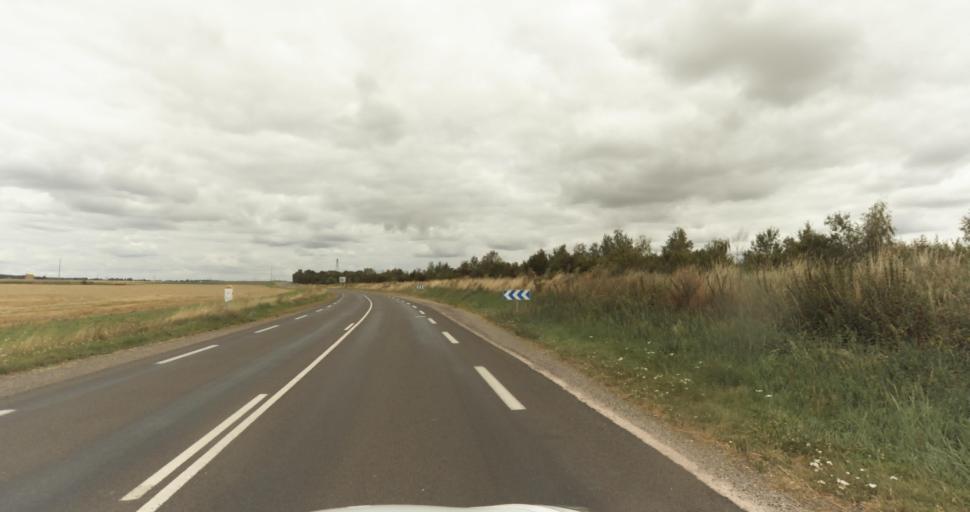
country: FR
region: Haute-Normandie
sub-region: Departement de l'Eure
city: La Madeleine-de-Nonancourt
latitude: 48.8313
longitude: 1.1843
